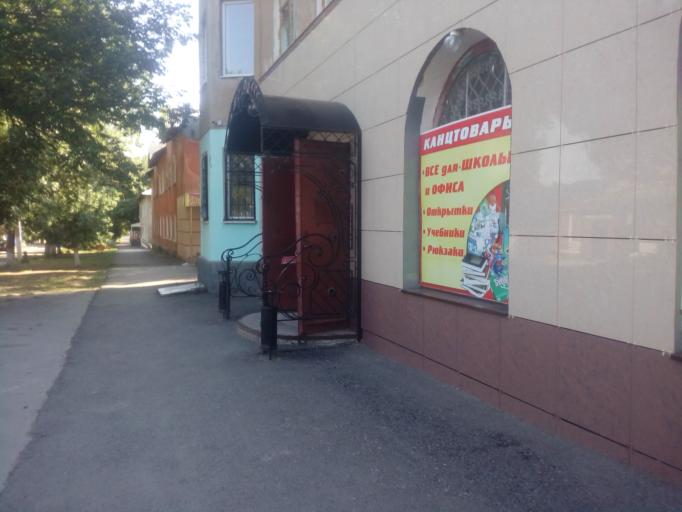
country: RU
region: Rostov
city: Sholokhovskiy
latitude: 48.2816
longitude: 41.0499
